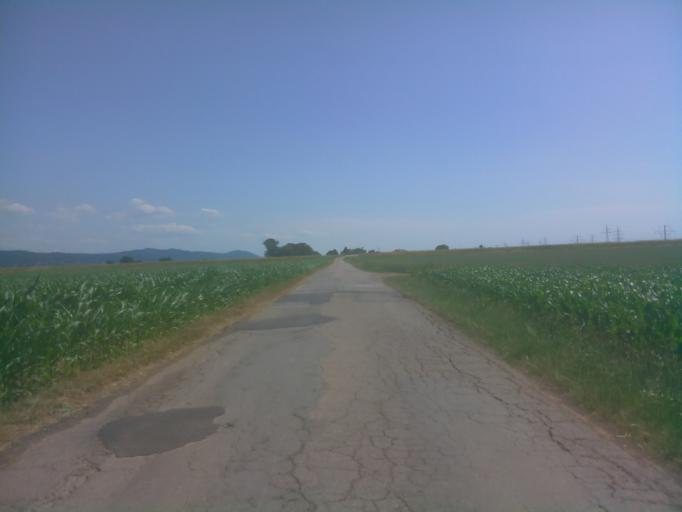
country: DE
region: Baden-Wuerttemberg
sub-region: Karlsruhe Region
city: Hemsbach
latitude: 49.5856
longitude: 8.6195
